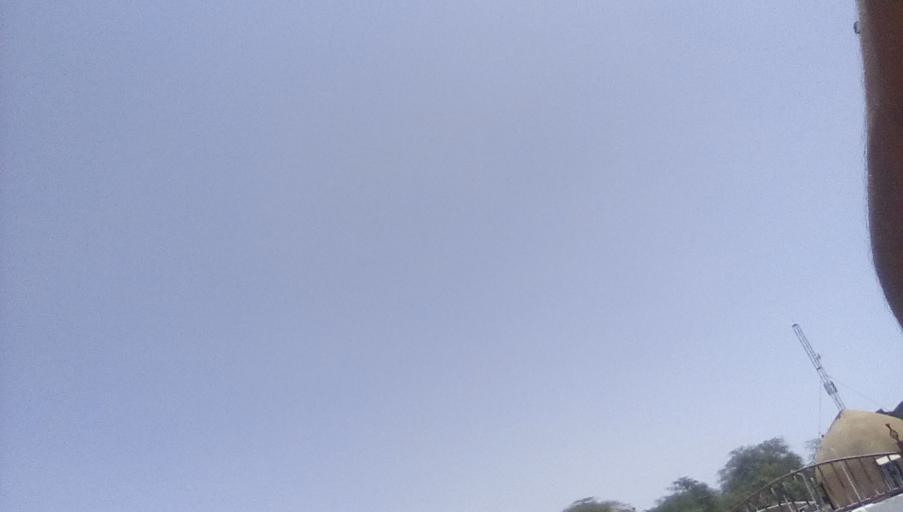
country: SN
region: Saint-Louis
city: Saint-Louis
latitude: 16.0660
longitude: -16.4228
